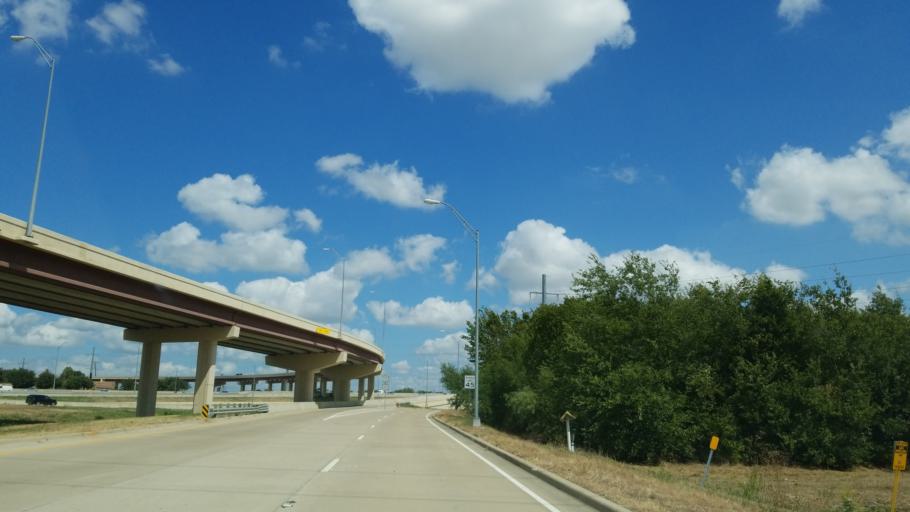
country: US
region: Texas
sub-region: Tarrant County
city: Grapevine
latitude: 32.9202
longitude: -97.0881
